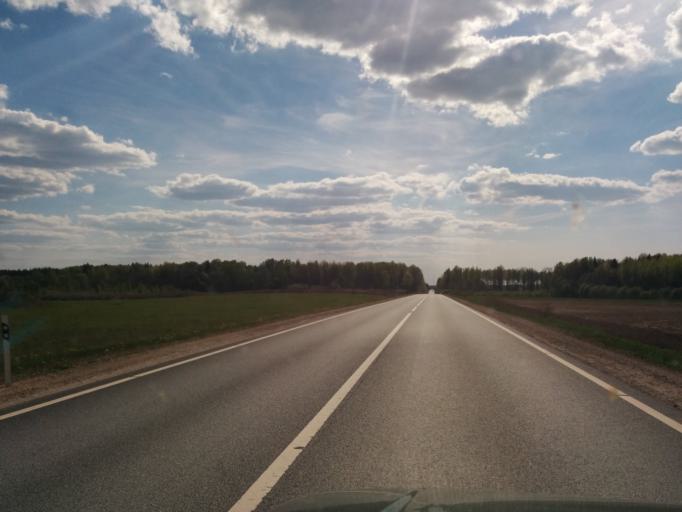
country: LV
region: Sigulda
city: Sigulda
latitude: 57.2378
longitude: 24.8267
